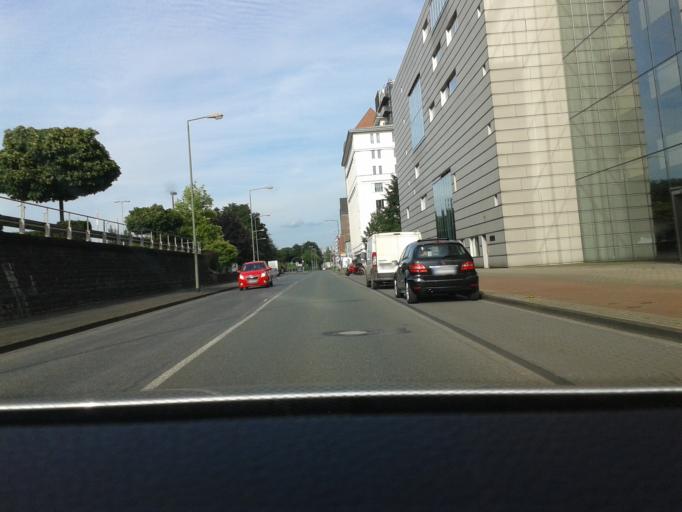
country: DE
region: North Rhine-Westphalia
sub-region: Regierungsbezirk Dusseldorf
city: Duisburg
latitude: 51.4355
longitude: 6.7541
